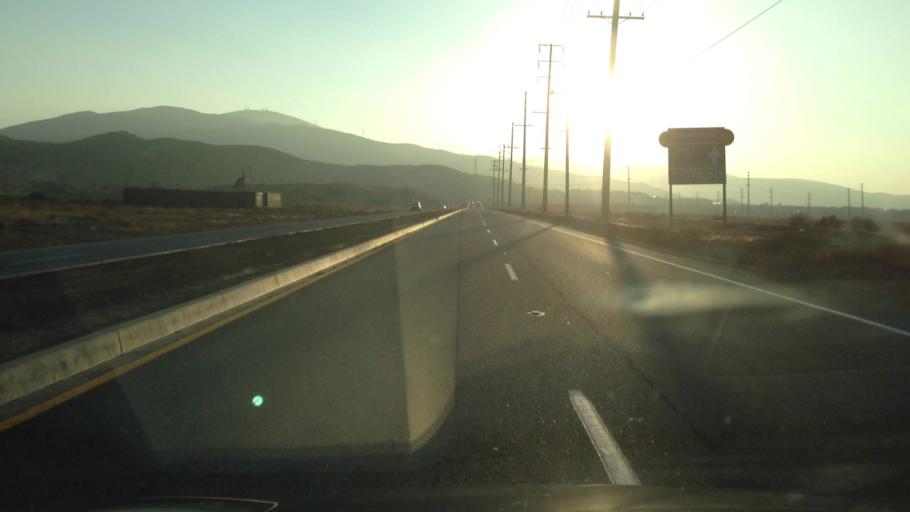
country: US
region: California
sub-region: Los Angeles County
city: Desert View Highlands
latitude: 34.5582
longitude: -118.1539
